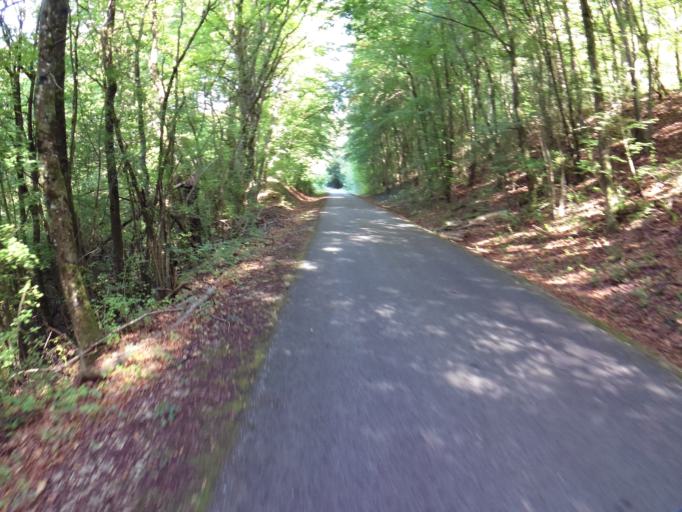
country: DE
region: Rheinland-Pfalz
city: Menningen
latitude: 49.8324
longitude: 6.4756
